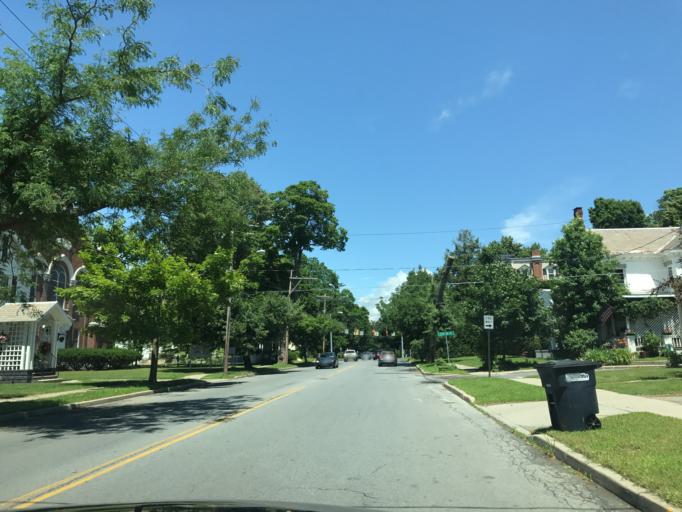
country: US
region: New York
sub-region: Warren County
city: Glens Falls
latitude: 43.3158
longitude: -73.6436
